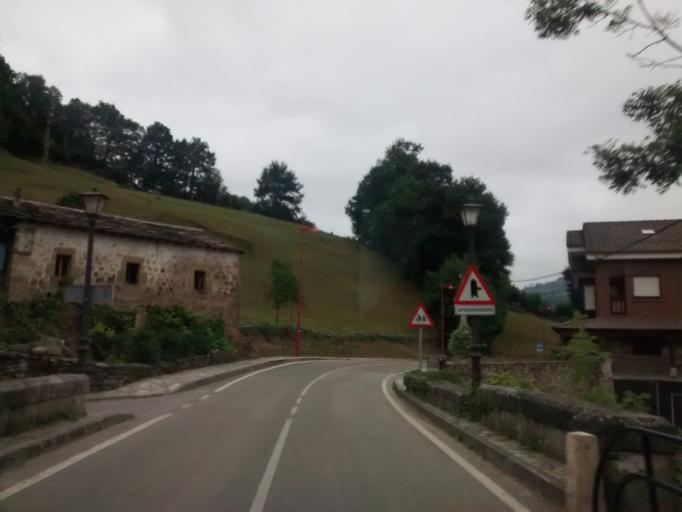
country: ES
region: Cantabria
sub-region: Provincia de Cantabria
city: Vega de Pas
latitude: 43.1563
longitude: -3.7843
